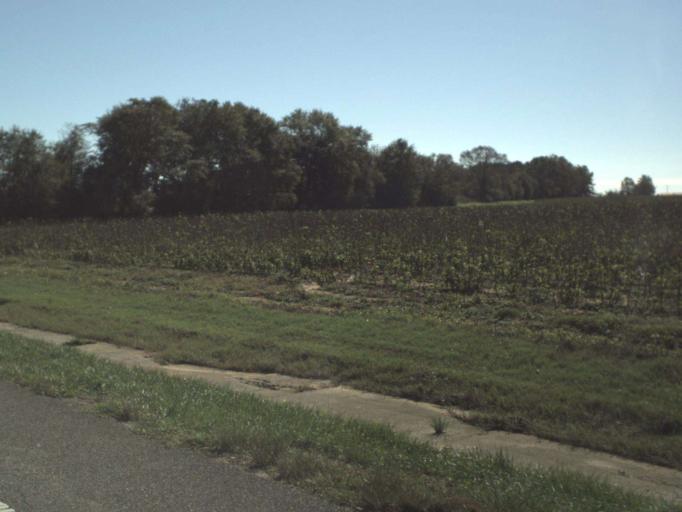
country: US
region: Florida
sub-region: Okaloosa County
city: Crestview
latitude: 30.8483
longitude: -86.7482
